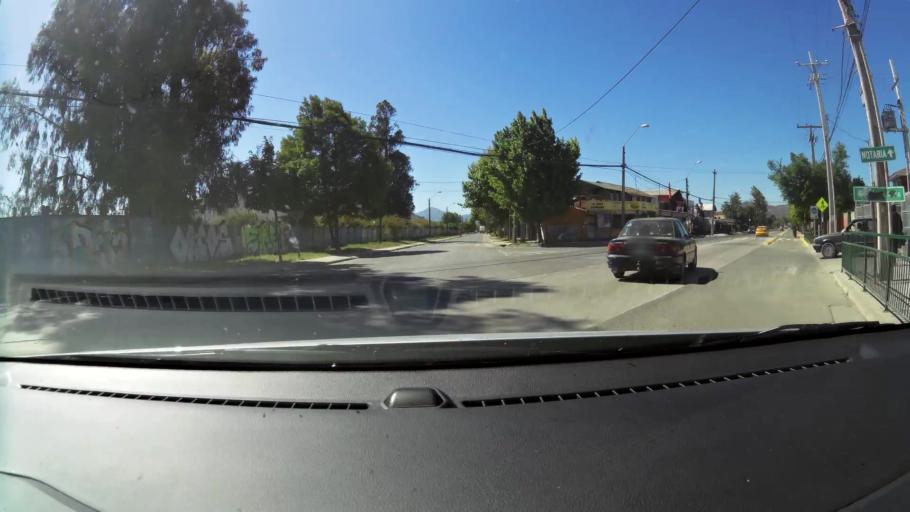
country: CL
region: Valparaiso
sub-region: Provincia de Marga Marga
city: Quilpue
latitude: -33.3111
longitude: -71.4094
